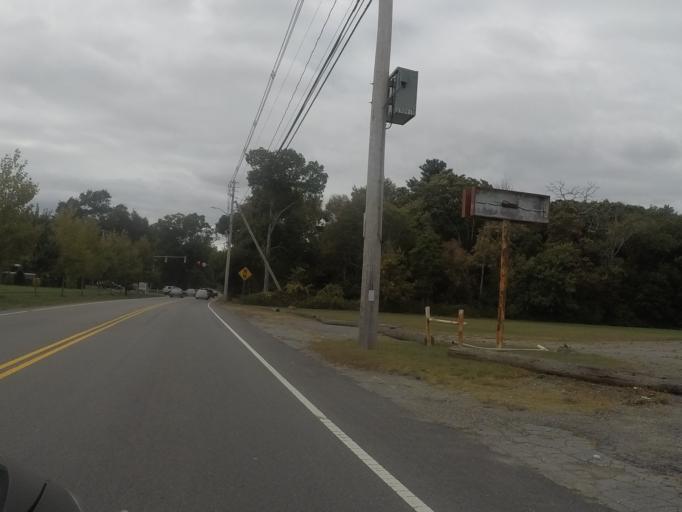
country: US
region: Massachusetts
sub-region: Bristol County
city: Smith Mills
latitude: 41.6739
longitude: -70.9889
